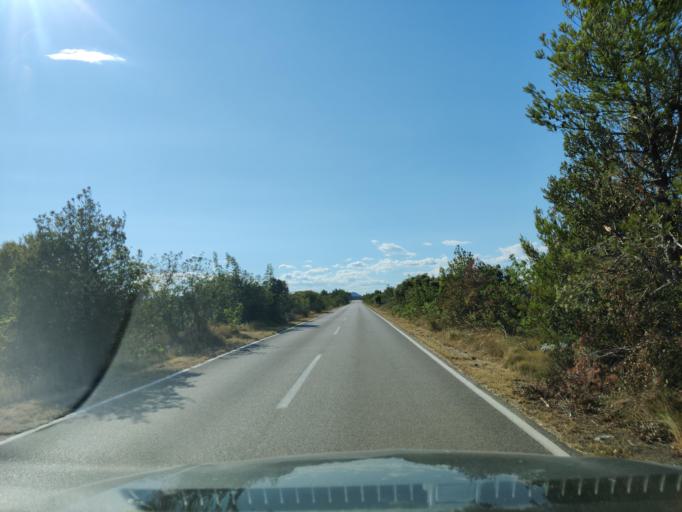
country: HR
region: Sibensko-Kniniska
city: Zaton
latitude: 43.7502
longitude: 15.8411
